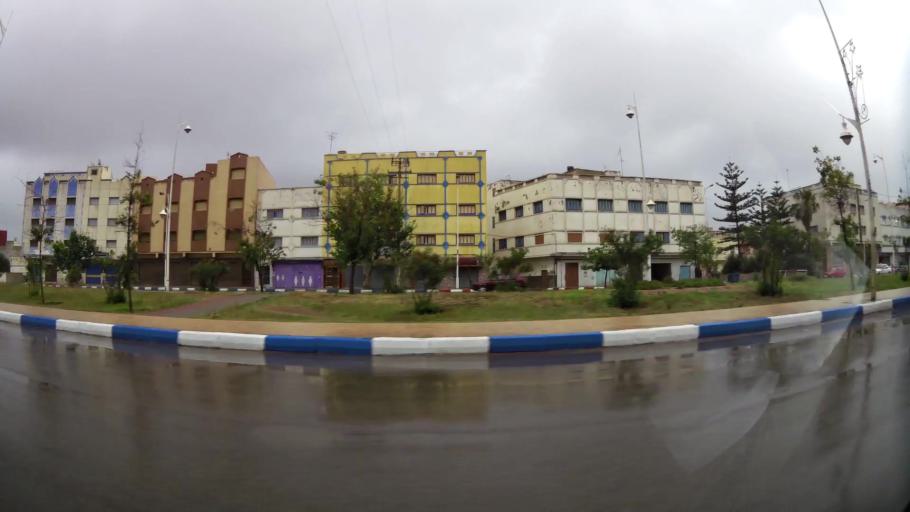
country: MA
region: Oriental
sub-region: Nador
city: Nador
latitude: 35.1687
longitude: -2.9437
